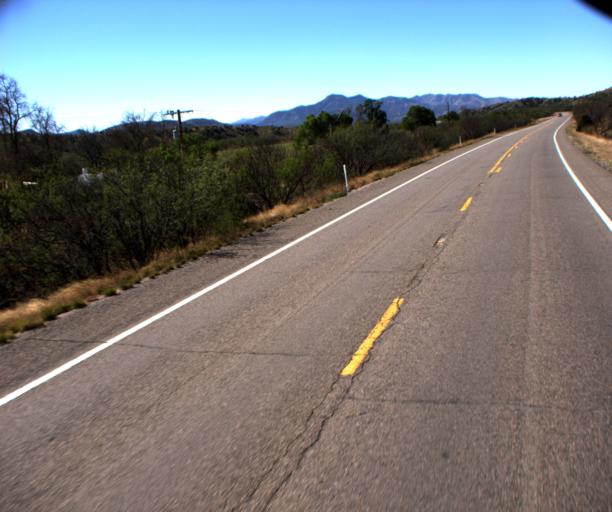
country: US
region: Arizona
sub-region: Santa Cruz County
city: Rio Rico
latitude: 31.6264
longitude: -110.7158
